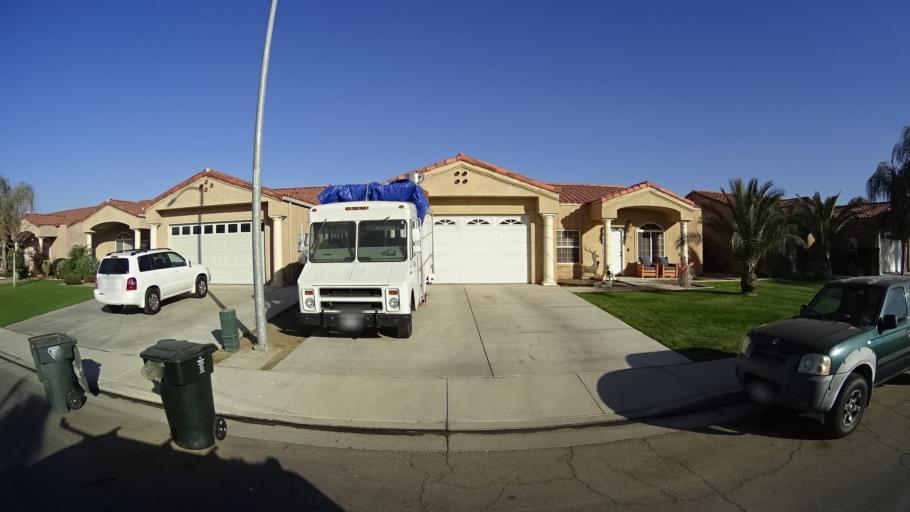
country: US
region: California
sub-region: Kern County
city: Greenfield
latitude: 35.2747
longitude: -119.0313
